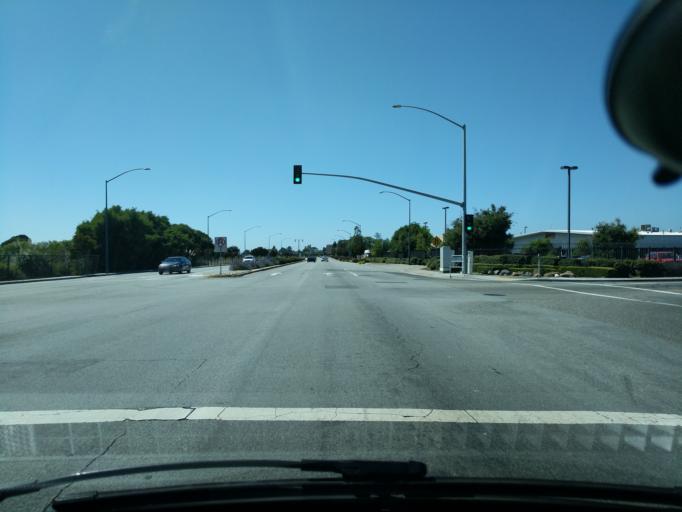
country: US
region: California
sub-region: Alameda County
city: San Leandro
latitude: 37.7222
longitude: -122.1942
